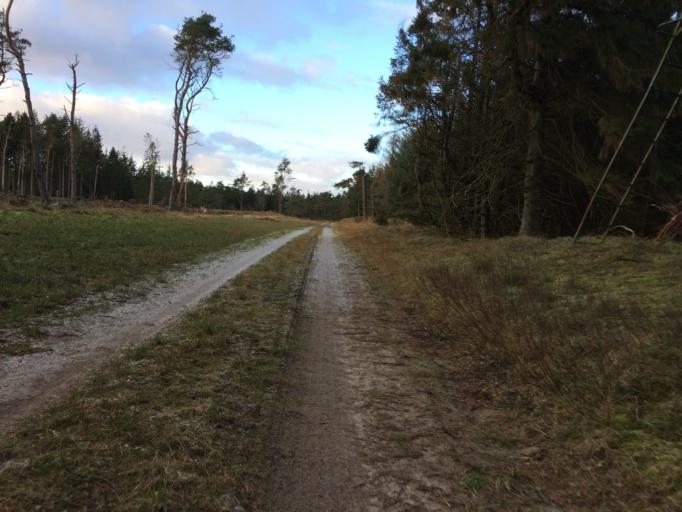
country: DK
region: Central Jutland
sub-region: Holstebro Kommune
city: Ulfborg
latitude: 56.2647
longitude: 8.3936
